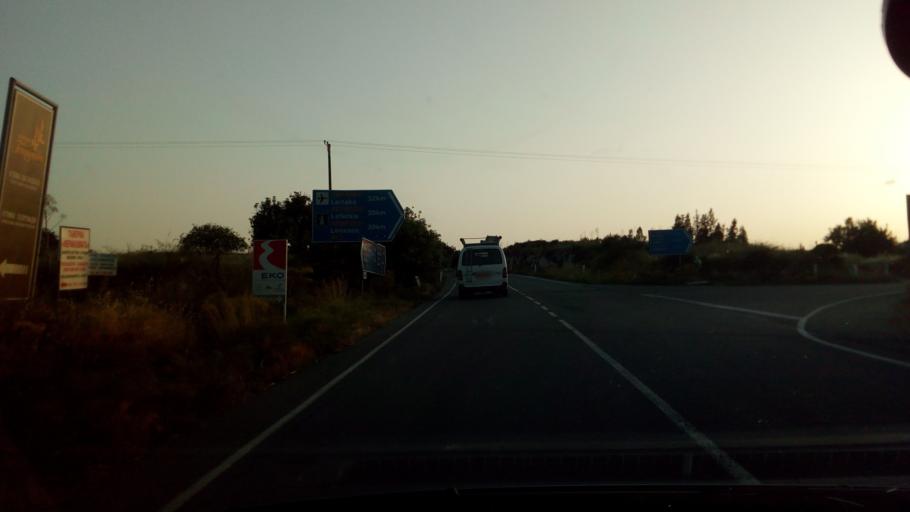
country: CY
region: Larnaka
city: Kofinou
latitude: 34.8148
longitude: 33.3645
